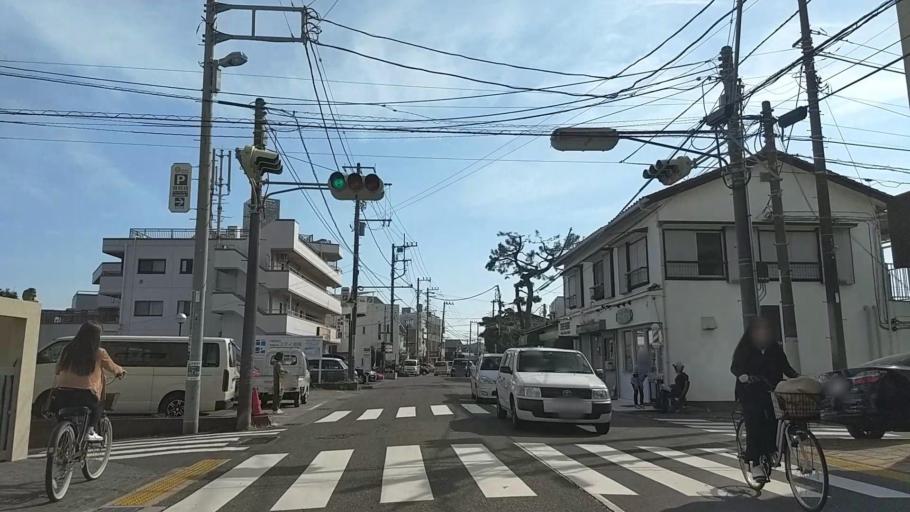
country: JP
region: Kanagawa
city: Fujisawa
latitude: 35.3242
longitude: 139.4538
